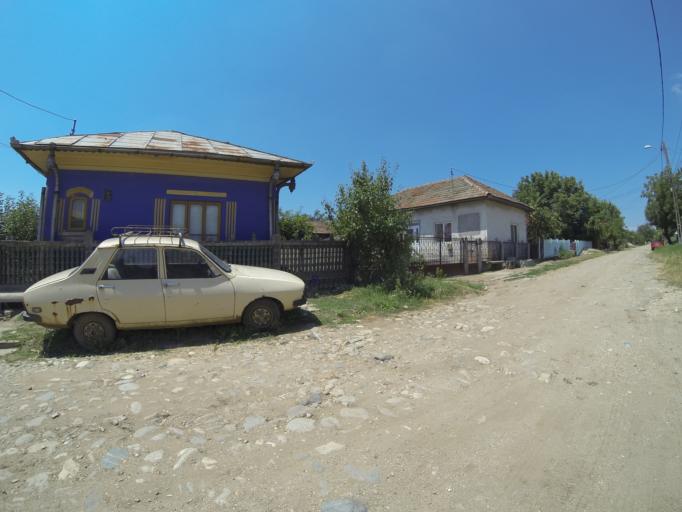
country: RO
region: Dolj
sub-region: Comuna Segarcea
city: Segarcea
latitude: 44.0882
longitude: 23.7485
